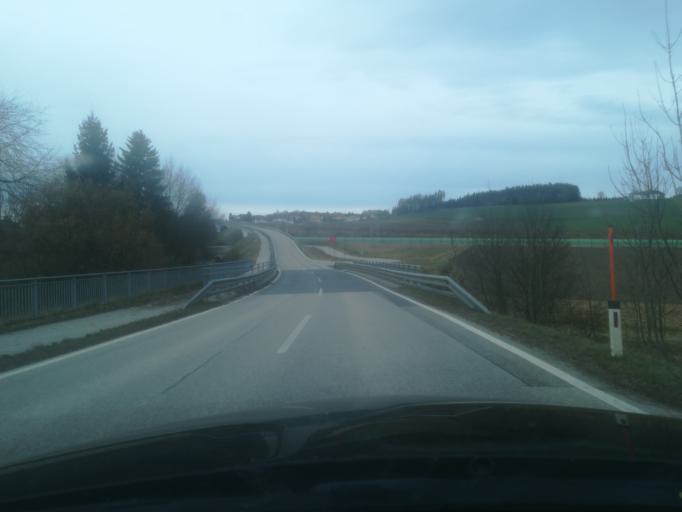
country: AT
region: Upper Austria
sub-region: Wels-Land
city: Neukirchen bei Lambach
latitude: 48.0934
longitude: 13.8386
